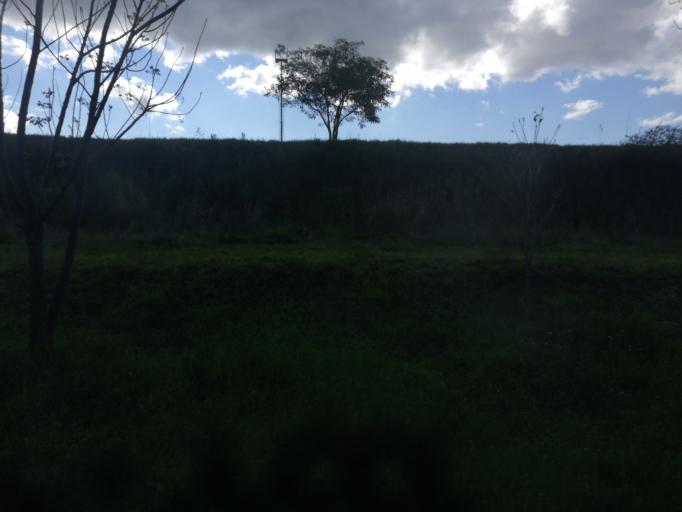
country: PY
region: Itapua
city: Encarnacion
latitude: -27.3647
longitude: -55.8523
